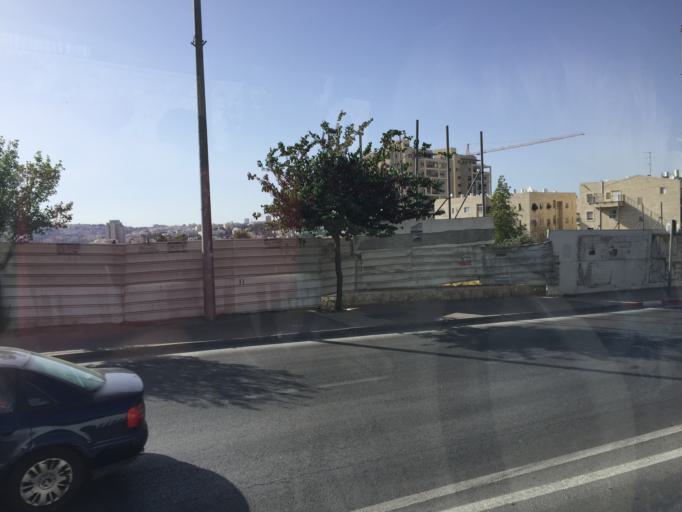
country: IL
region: Jerusalem
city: Jerusalem
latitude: 31.7442
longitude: 35.2155
